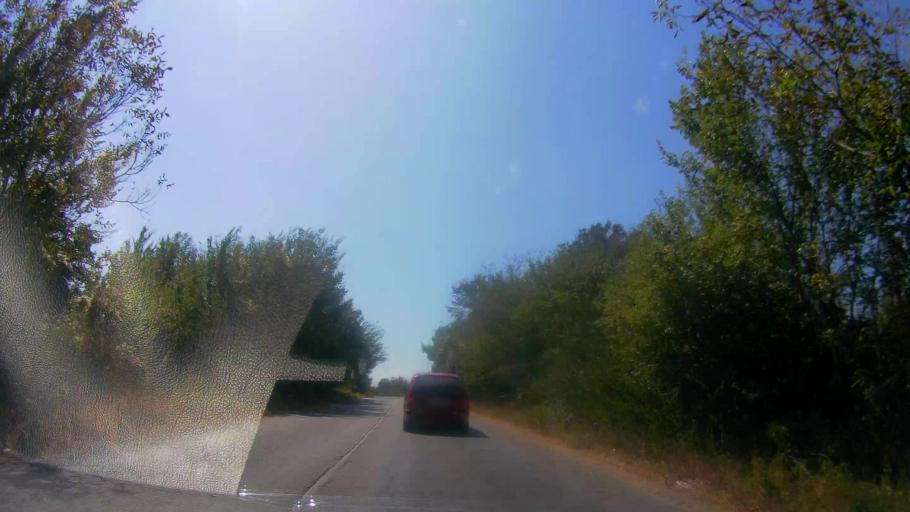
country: BG
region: Veliko Turnovo
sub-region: Obshtina Gorna Oryakhovitsa
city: Purvomaytsi
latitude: 43.2374
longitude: 25.6410
